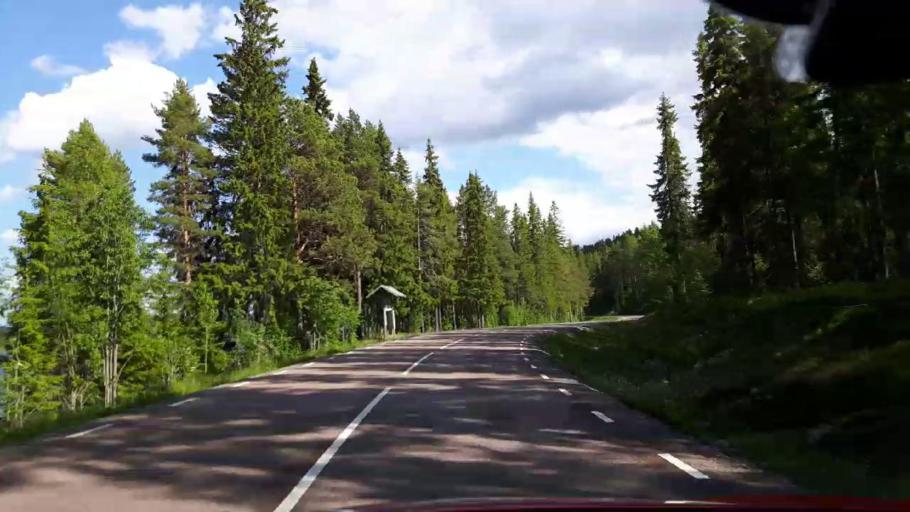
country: SE
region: Jaemtland
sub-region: Krokoms Kommun
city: Valla
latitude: 63.9591
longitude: 14.1889
